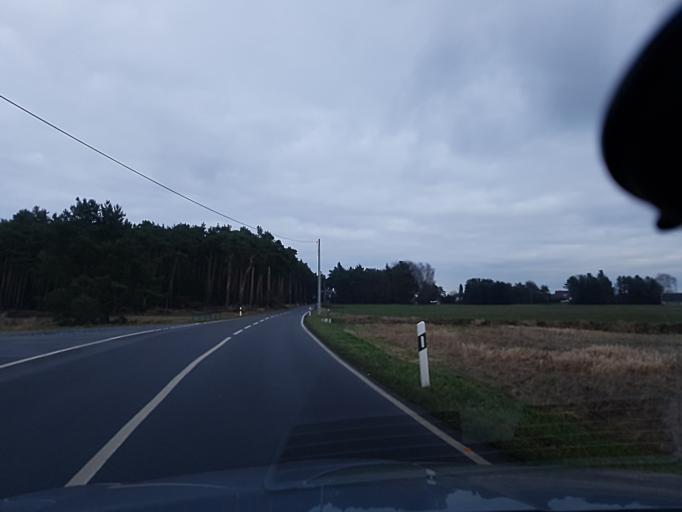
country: DE
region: Brandenburg
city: Bad Liebenwerda
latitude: 51.5465
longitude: 13.3195
